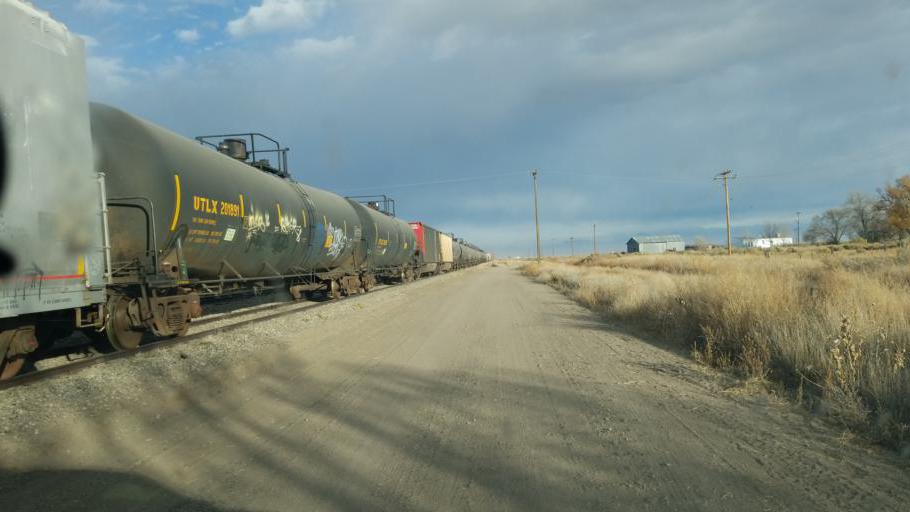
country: US
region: Colorado
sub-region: Alamosa County
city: Alamosa East
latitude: 37.4658
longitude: -105.8410
